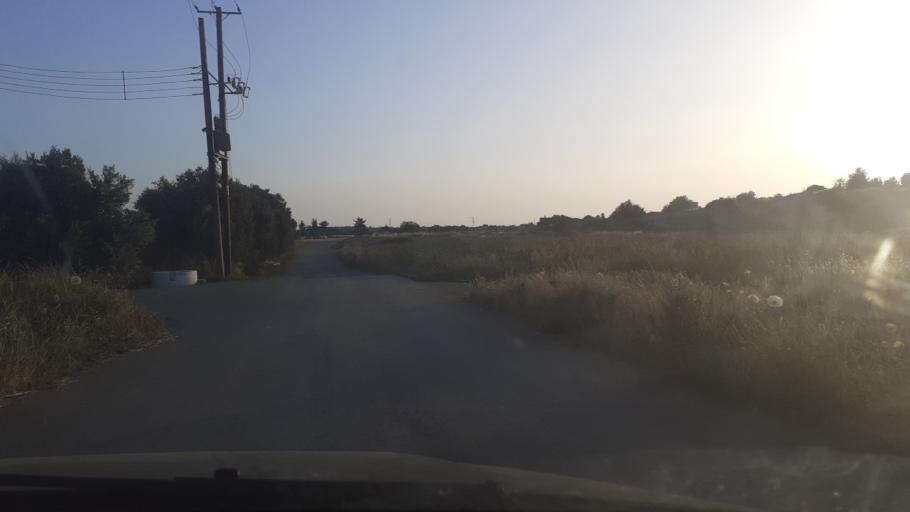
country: CY
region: Larnaka
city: Kolossi
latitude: 34.6694
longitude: 32.9462
